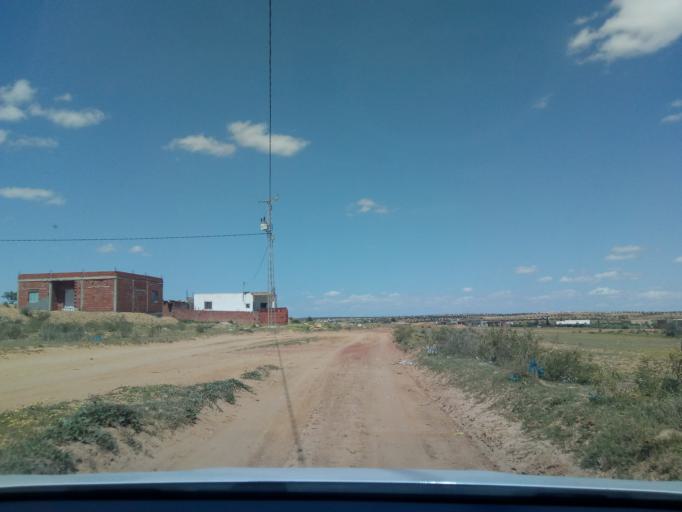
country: TN
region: Safaqis
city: Sfax
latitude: 34.7299
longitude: 10.4979
